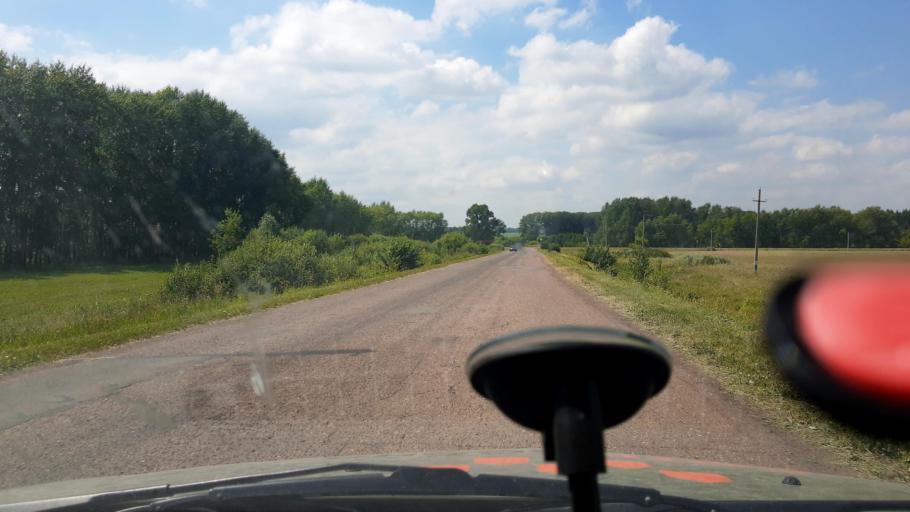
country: RU
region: Bashkortostan
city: Chekmagush
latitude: 54.8880
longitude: 54.5822
